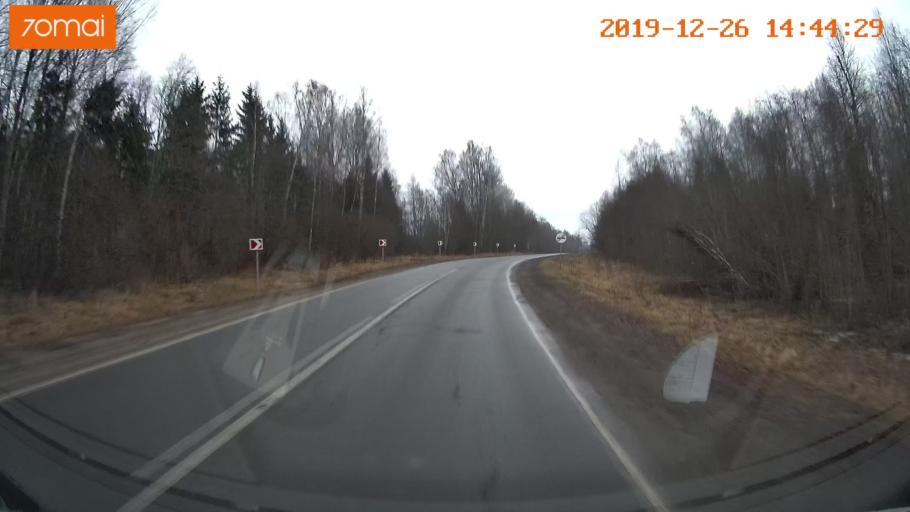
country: RU
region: Jaroslavl
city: Poshekhon'ye
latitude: 58.3475
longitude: 39.0510
